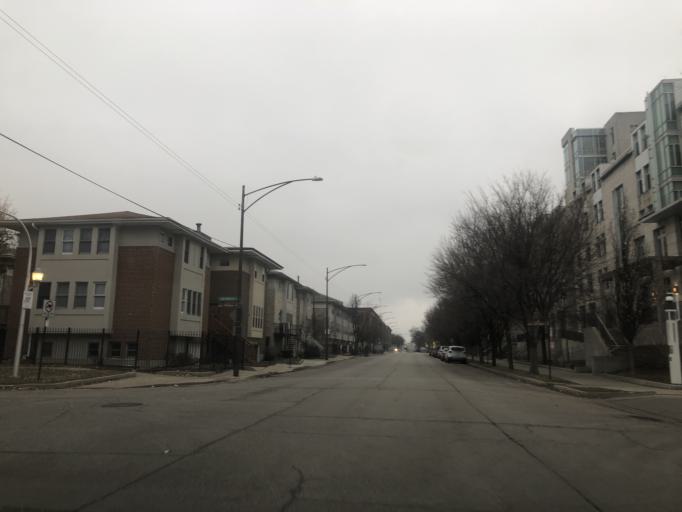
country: US
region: Illinois
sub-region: Cook County
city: Chicago
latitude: 41.7842
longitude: -87.5992
